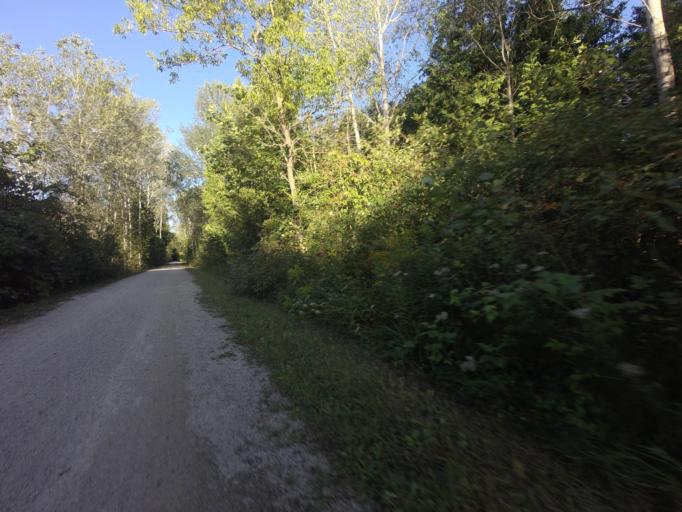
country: CA
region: Ontario
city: Orangeville
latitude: 43.8243
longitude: -79.9162
